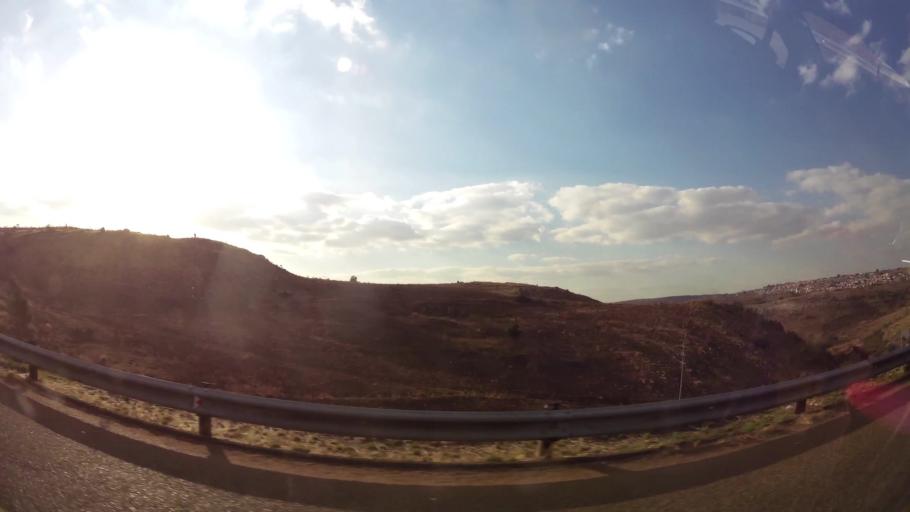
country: ZA
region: Gauteng
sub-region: West Rand District Municipality
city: Krugersdorp
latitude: -26.0854
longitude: 27.7414
